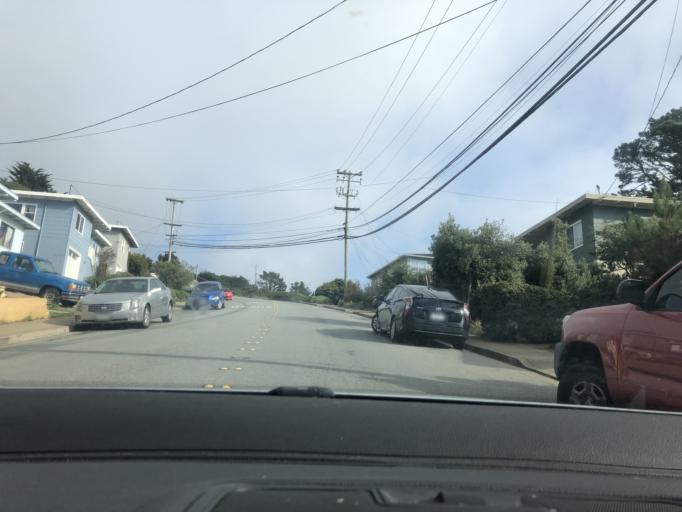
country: US
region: California
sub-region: San Mateo County
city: Pacifica
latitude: 37.6461
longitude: -122.4777
